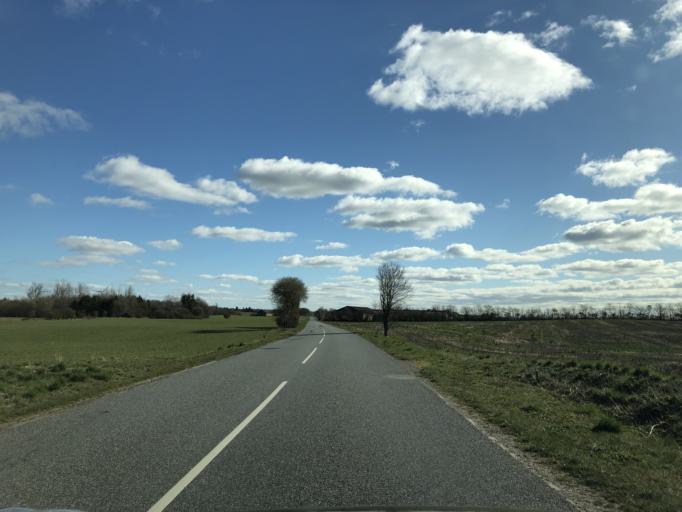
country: DK
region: North Denmark
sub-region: Vesthimmerland Kommune
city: Alestrup
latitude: 56.6108
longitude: 9.5983
